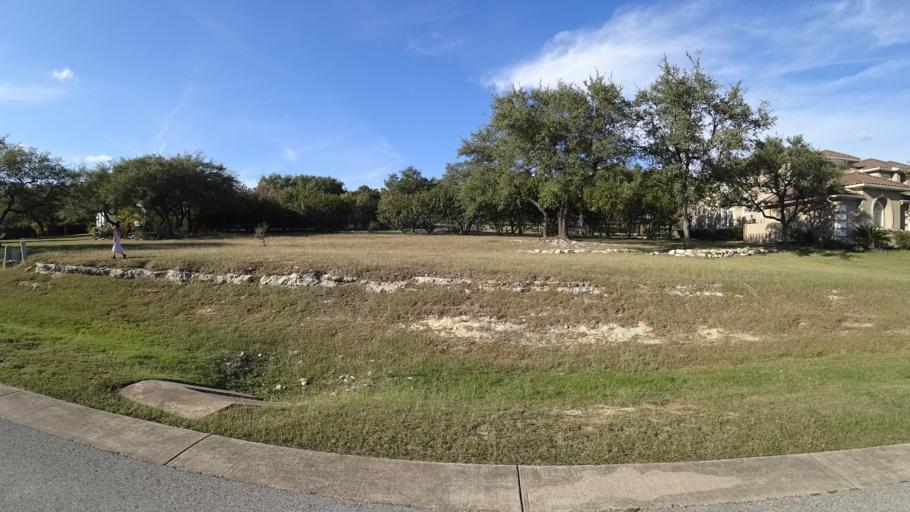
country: US
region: Texas
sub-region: Travis County
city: Barton Creek
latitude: 30.2574
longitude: -97.8451
